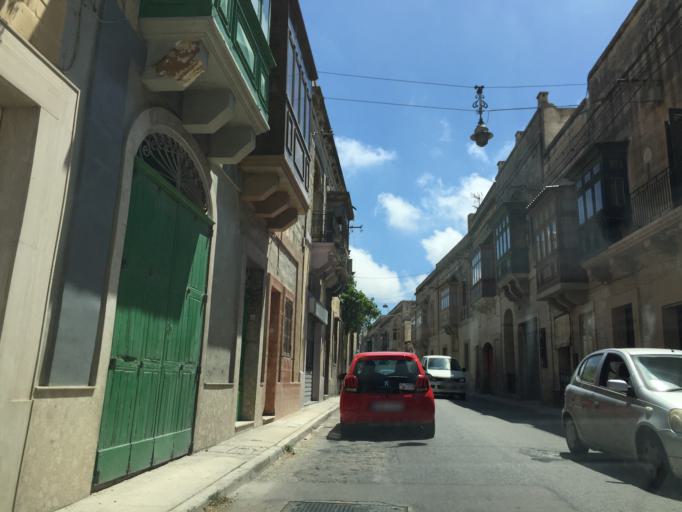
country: MT
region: Ir-Rabat
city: Rabat
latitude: 35.8802
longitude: 14.4010
